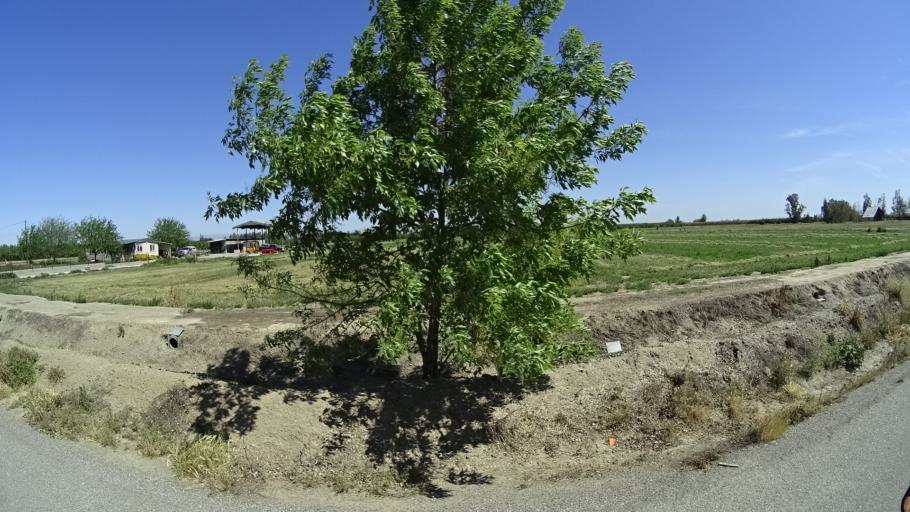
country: US
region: California
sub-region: Glenn County
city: Orland
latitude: 39.7421
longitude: -122.1504
